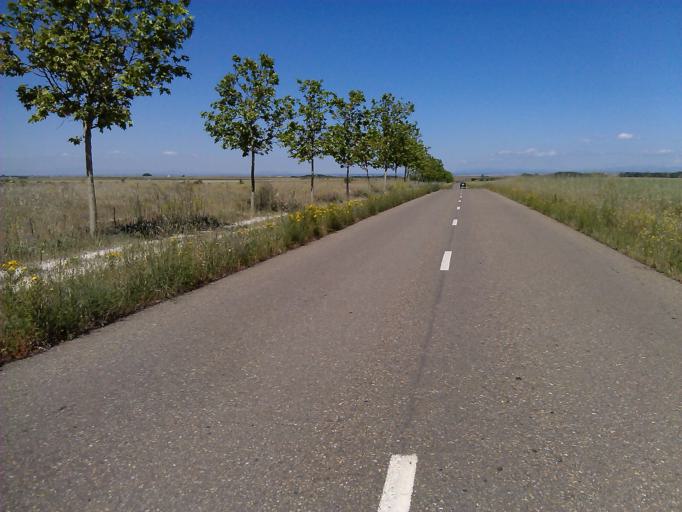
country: ES
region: Castille and Leon
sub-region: Provincia de Leon
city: Villamoratiel de las Matas
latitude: 42.4610
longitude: -5.3022
